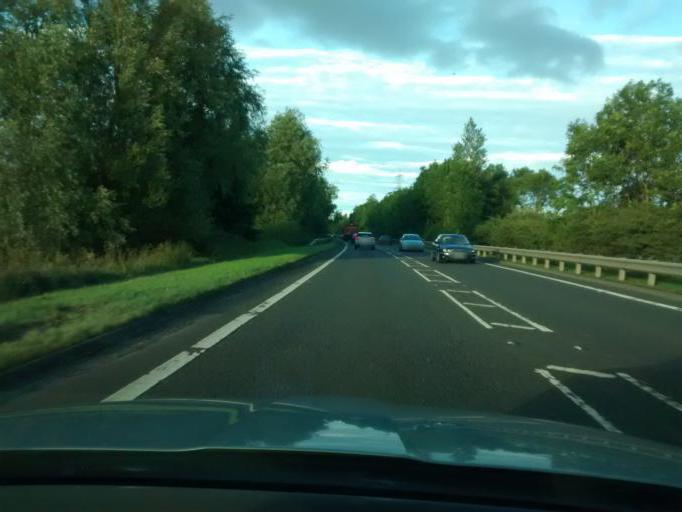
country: GB
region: Scotland
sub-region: Renfrewshire
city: Howwood
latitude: 55.8145
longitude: -4.5543
